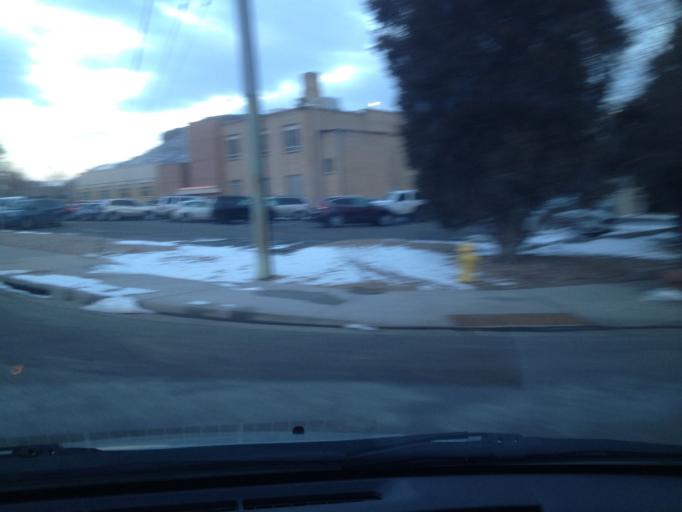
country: US
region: Colorado
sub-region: Jefferson County
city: Golden
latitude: 39.7584
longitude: -105.2241
